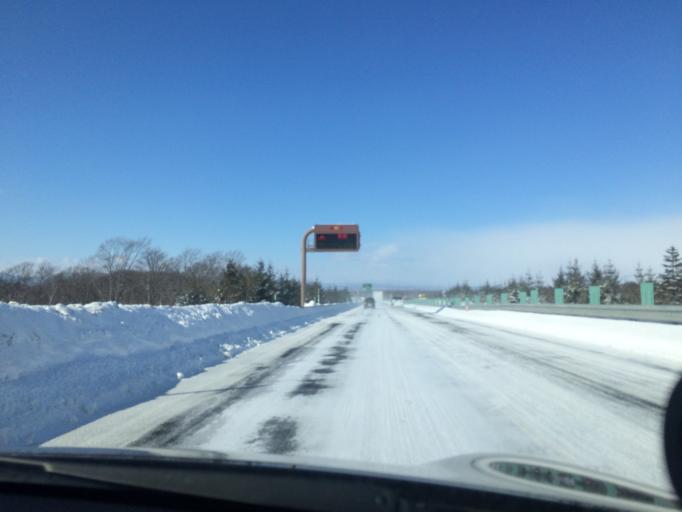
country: JP
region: Hokkaido
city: Chitose
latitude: 42.8804
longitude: 141.7183
